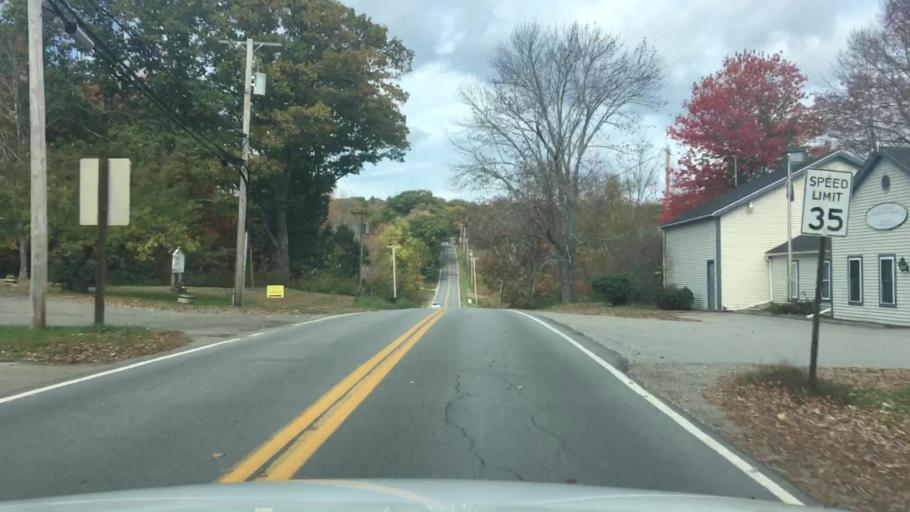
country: US
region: Maine
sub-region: Knox County
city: Hope
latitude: 44.2989
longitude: -69.1085
